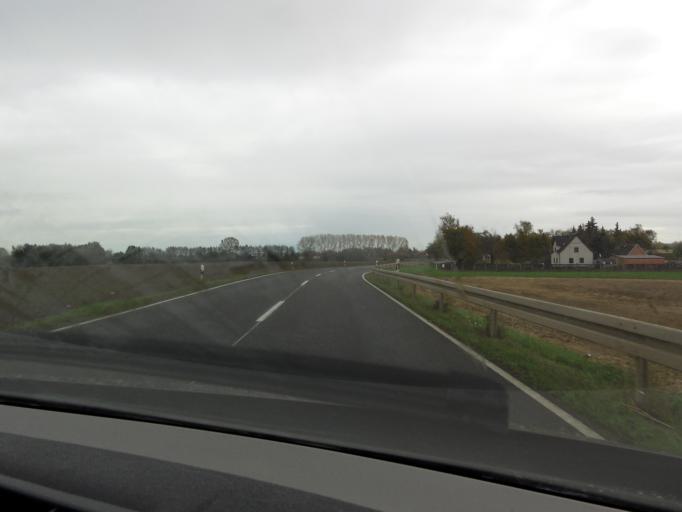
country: DE
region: Saxony
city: Elstertrebnitz
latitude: 51.1195
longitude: 12.2031
